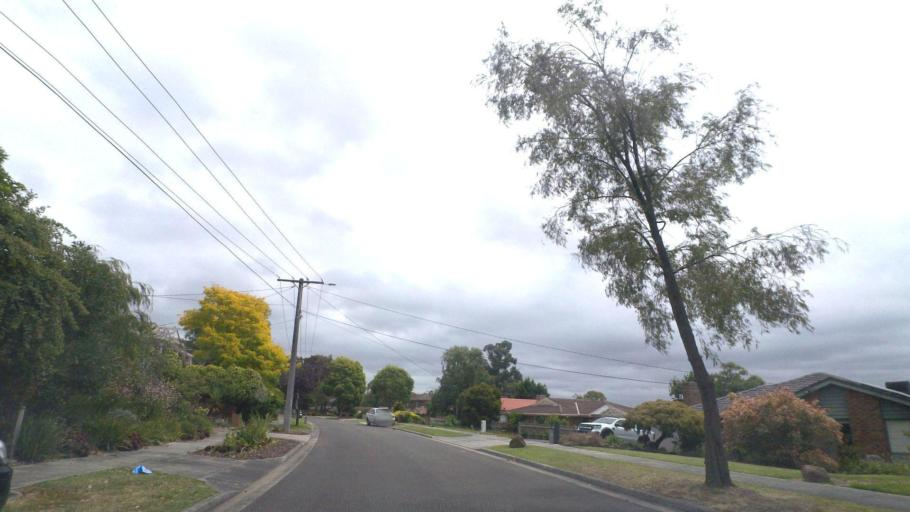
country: AU
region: Victoria
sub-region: Knox
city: The Basin
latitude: -37.8590
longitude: 145.3045
